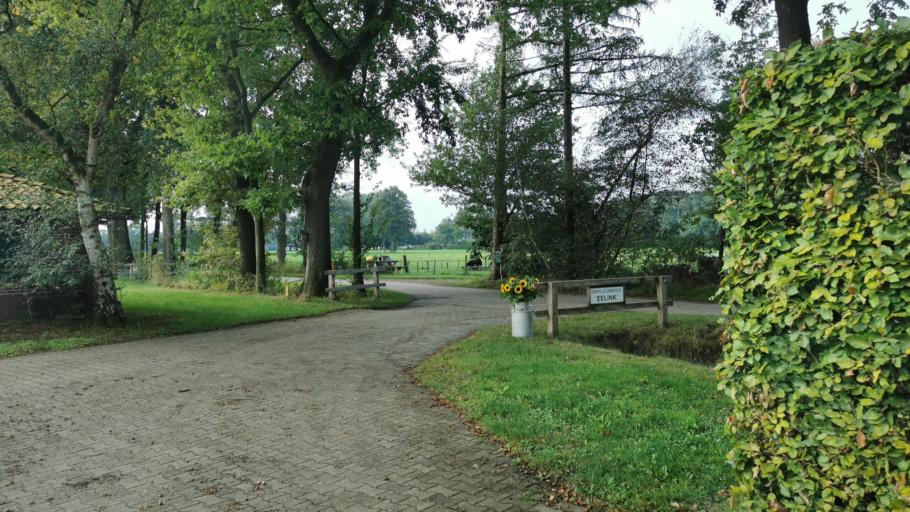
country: NL
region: Gelderland
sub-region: Gemeente Winterswijk
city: Winterswijk
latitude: 51.9278
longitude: 6.6878
